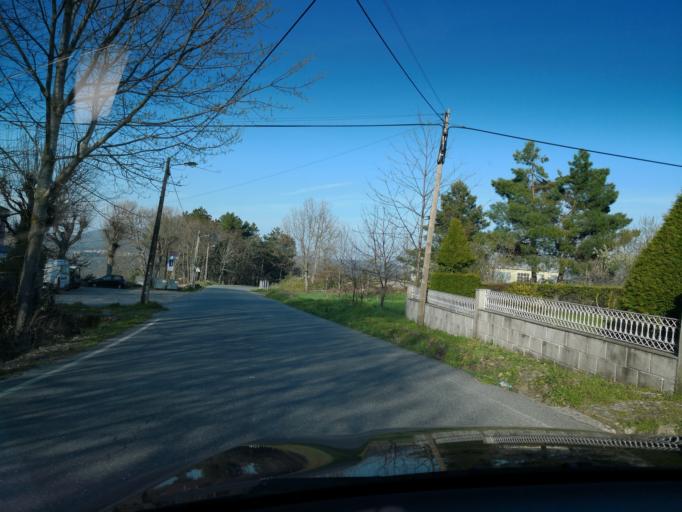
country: PT
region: Vila Real
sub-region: Sabrosa
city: Sabrosa
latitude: 41.3566
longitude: -7.6198
